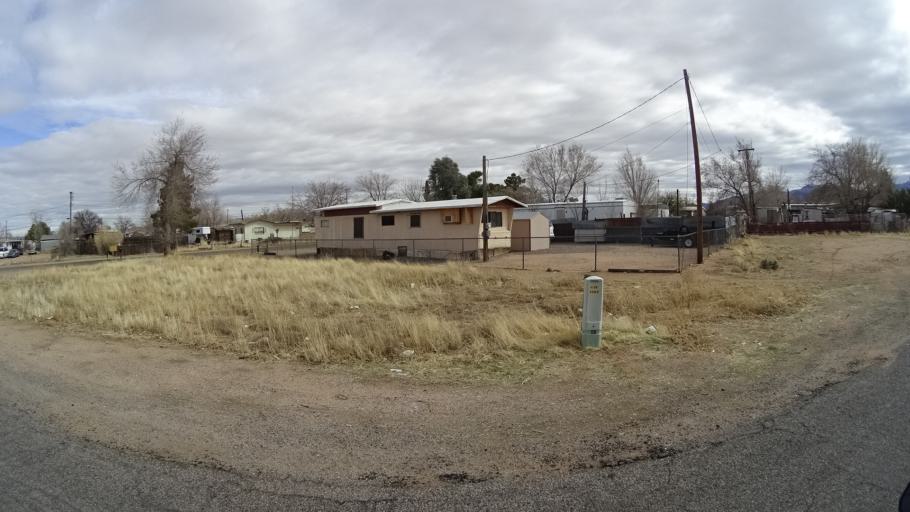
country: US
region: Arizona
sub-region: Mohave County
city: New Kingman-Butler
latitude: 35.2448
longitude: -113.9933
